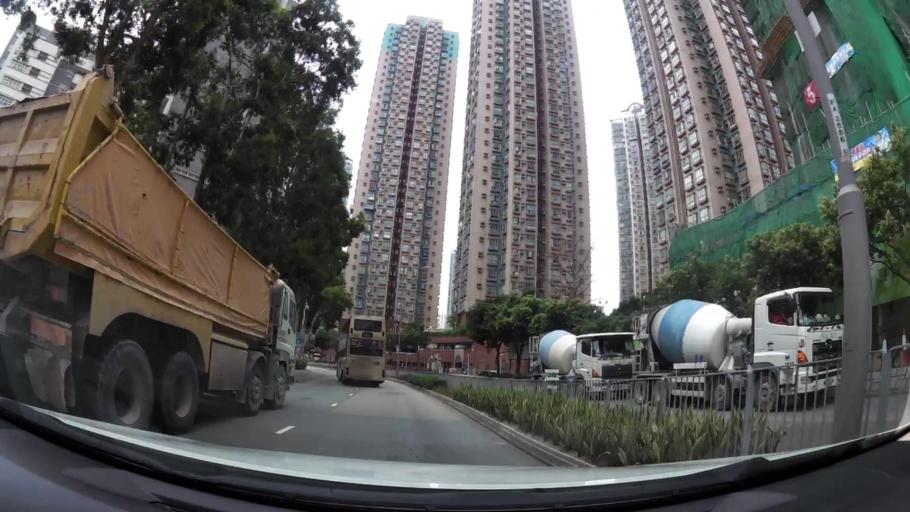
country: HK
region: Tuen Mun
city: Tuen Mun
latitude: 22.4092
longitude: 113.9685
